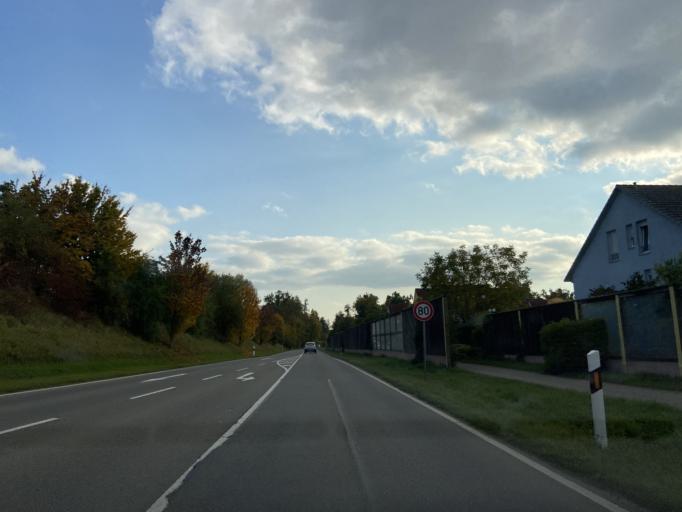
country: DE
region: Baden-Wuerttemberg
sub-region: Tuebingen Region
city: Sigmaringen
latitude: 48.0905
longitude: 9.2411
